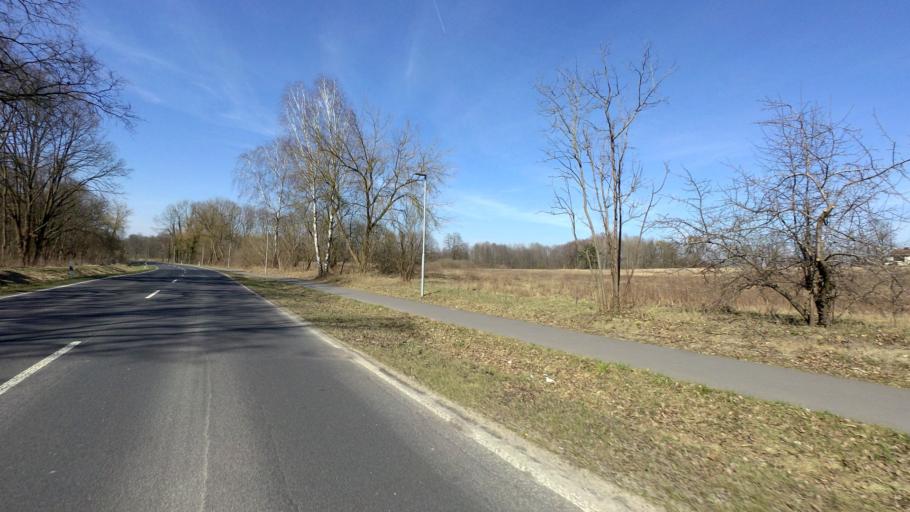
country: DE
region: Brandenburg
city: Muncheberg
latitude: 52.5198
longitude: 14.1084
